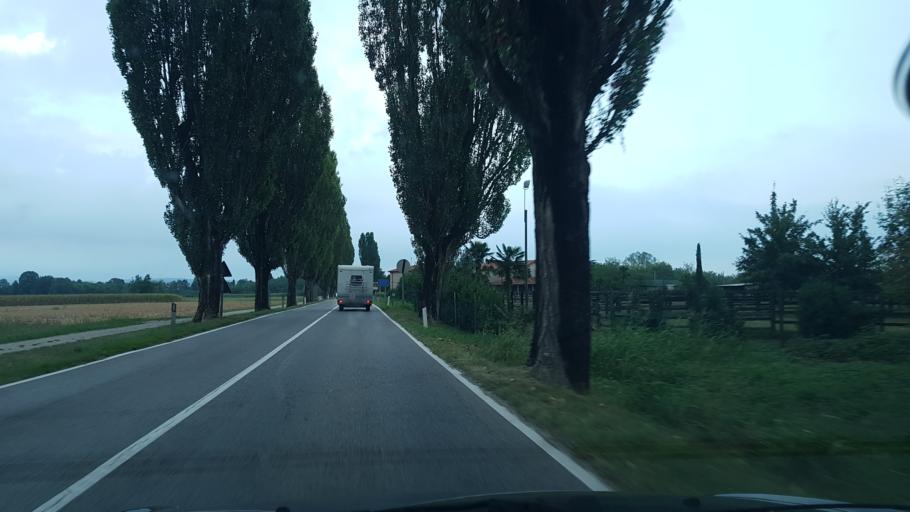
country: IT
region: Friuli Venezia Giulia
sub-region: Provincia di Gorizia
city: Romans d'Isonzo
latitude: 45.8966
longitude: 13.4243
